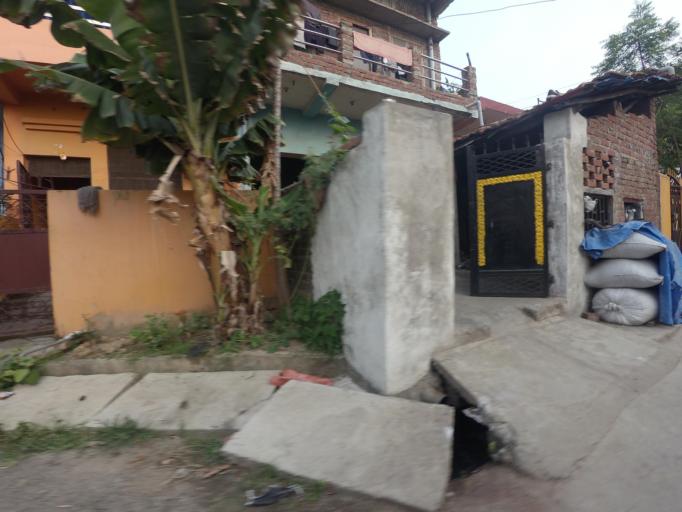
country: NP
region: Western Region
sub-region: Lumbini Zone
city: Bhairahawa
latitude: 27.5137
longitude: 83.4470
